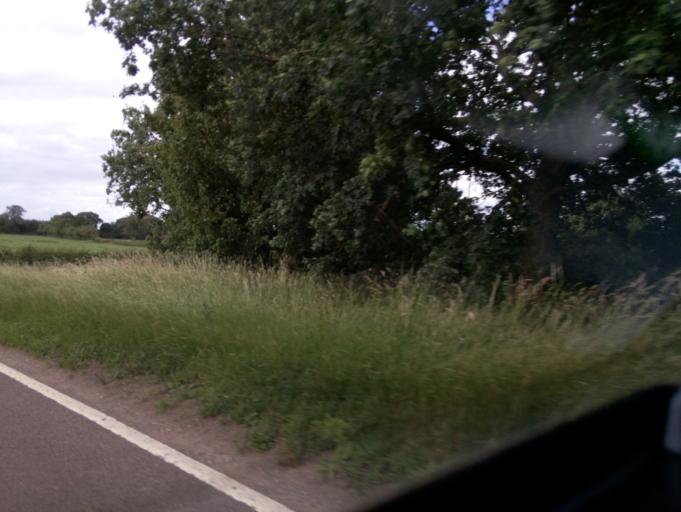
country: GB
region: England
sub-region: Leicestershire
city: Donisthorpe
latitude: 52.6836
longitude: -1.5454
